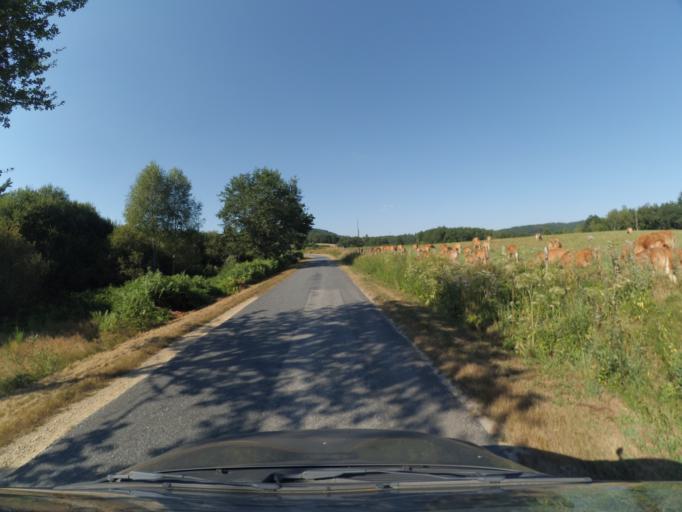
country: FR
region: Limousin
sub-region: Departement de la Haute-Vienne
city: Eymoutiers
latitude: 45.7461
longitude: 1.8199
